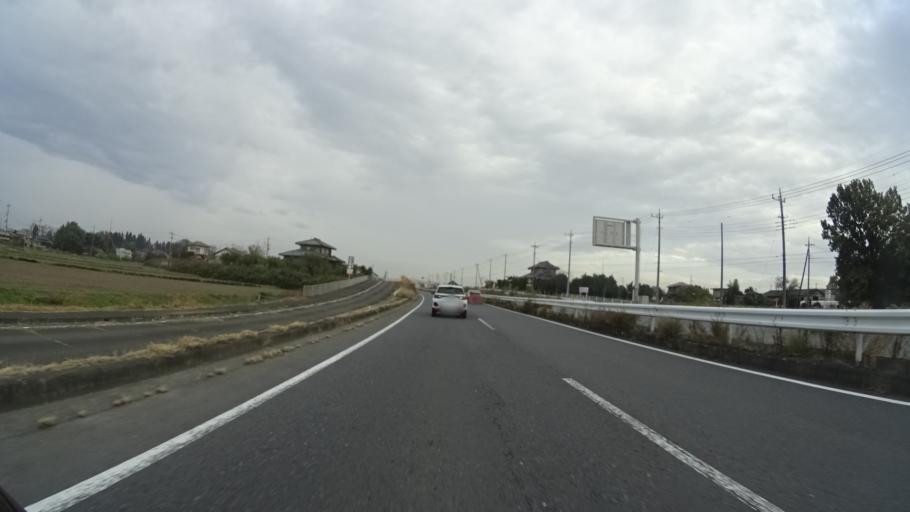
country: JP
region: Gunma
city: Isesaki
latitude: 36.3645
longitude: 139.1629
